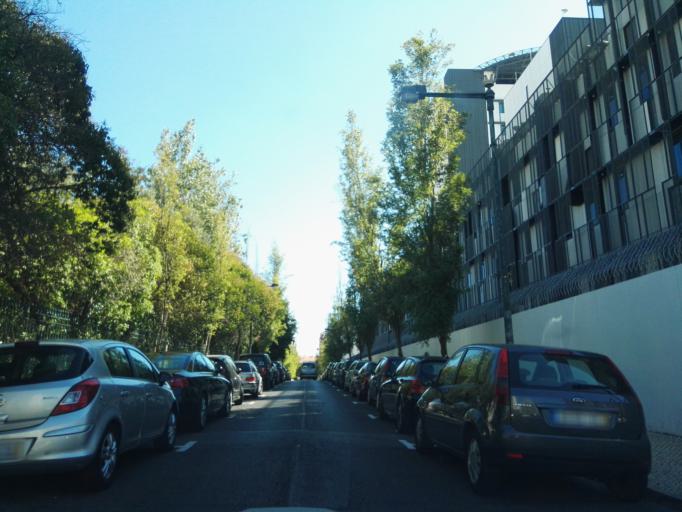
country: PT
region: Lisbon
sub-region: Lisbon
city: Lisbon
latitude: 38.7293
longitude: -9.1433
